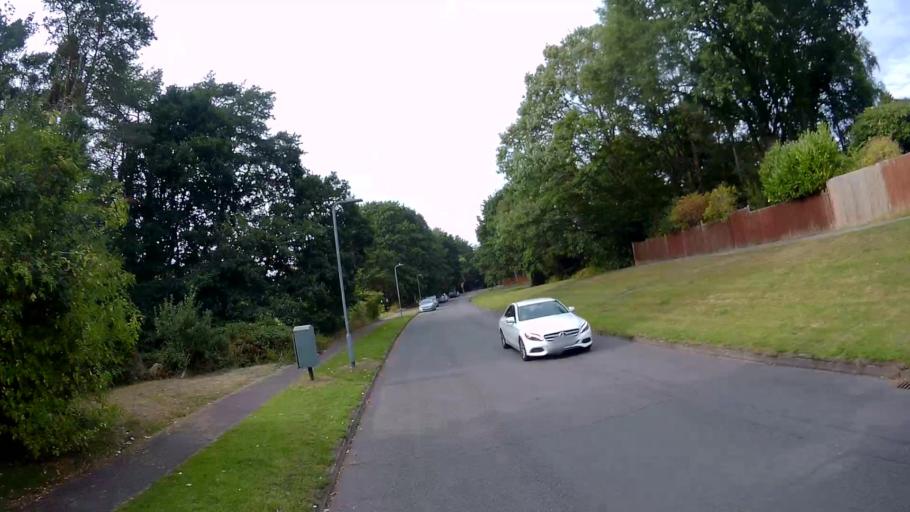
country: GB
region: England
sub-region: Bracknell Forest
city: Crowthorne
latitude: 51.3889
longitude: -0.7737
